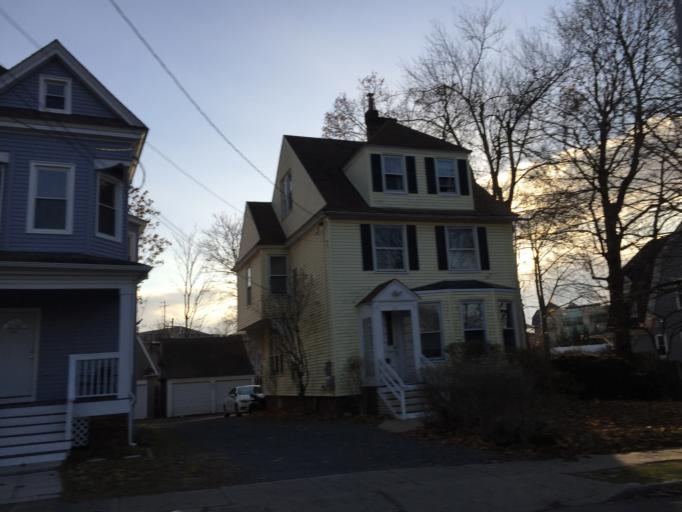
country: US
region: New Jersey
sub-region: Union County
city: Summit
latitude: 40.7182
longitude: -74.3624
